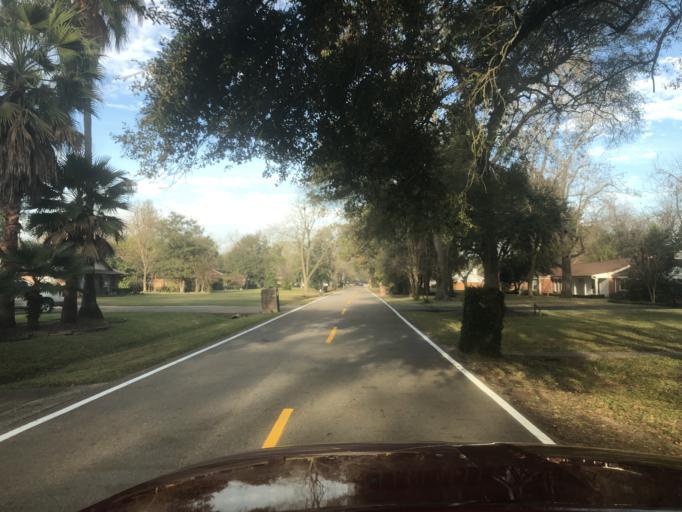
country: US
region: Texas
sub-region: Harris County
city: Spring
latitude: 30.0121
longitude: -95.4688
